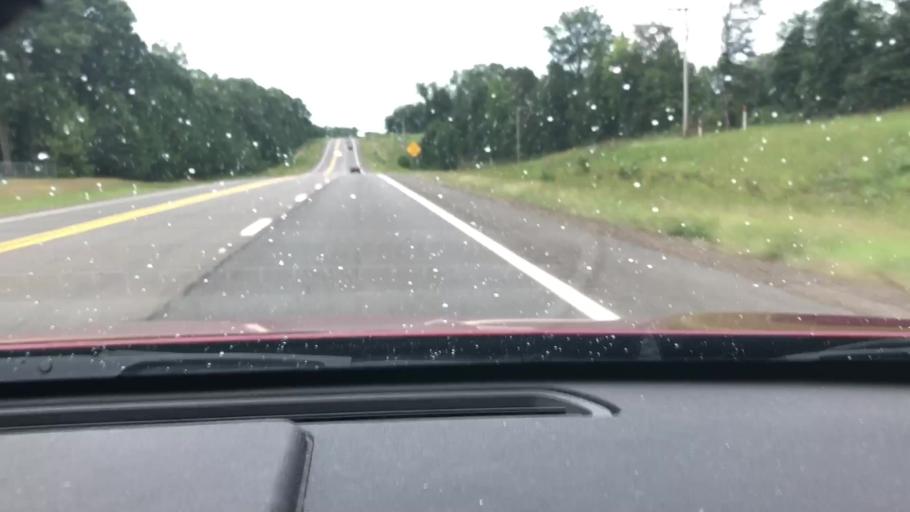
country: US
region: Arkansas
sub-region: Columbia County
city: Waldo
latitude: 33.3510
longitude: -93.3739
